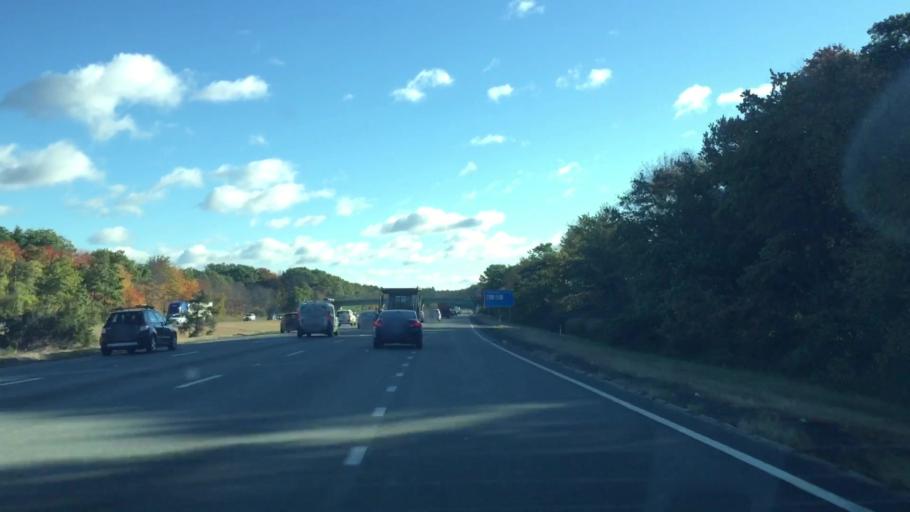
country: US
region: Massachusetts
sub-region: Middlesex County
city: Tewksbury
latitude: 42.6293
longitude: -71.2673
